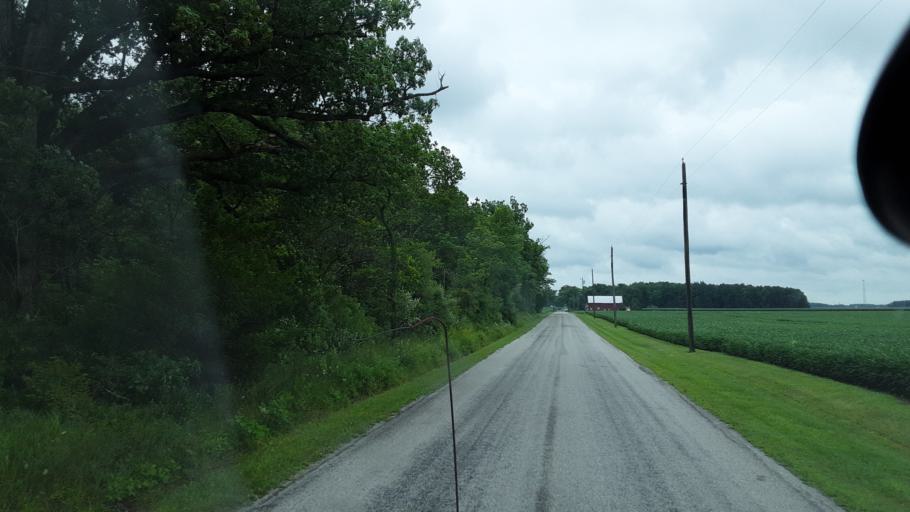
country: US
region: Indiana
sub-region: Wells County
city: Ossian
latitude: 40.8206
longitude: -85.0720
